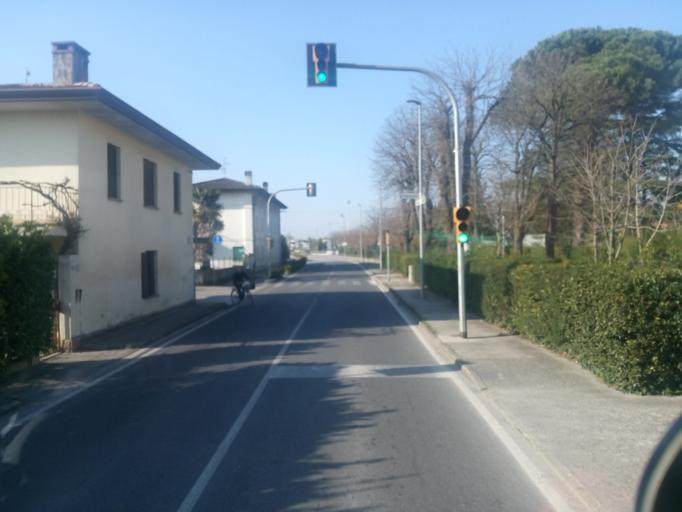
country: IT
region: Friuli Venezia Giulia
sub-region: Provincia di Udine
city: Castions di Strada
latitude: 45.9105
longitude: 13.1825
